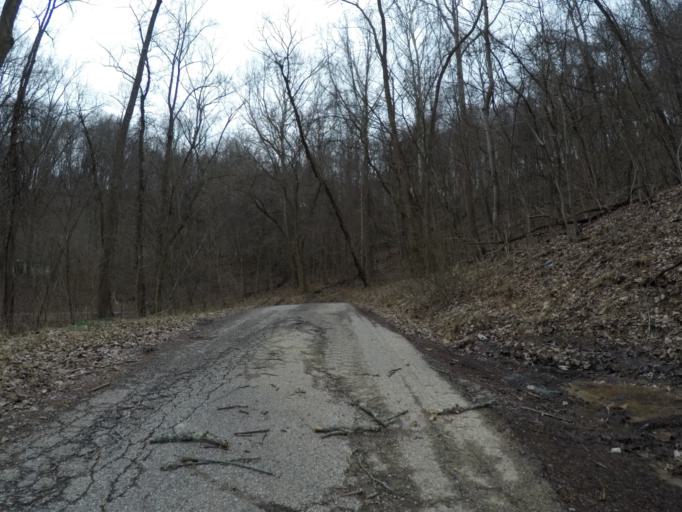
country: US
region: Ohio
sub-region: Lawrence County
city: Burlington
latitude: 38.3907
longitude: -82.5183
